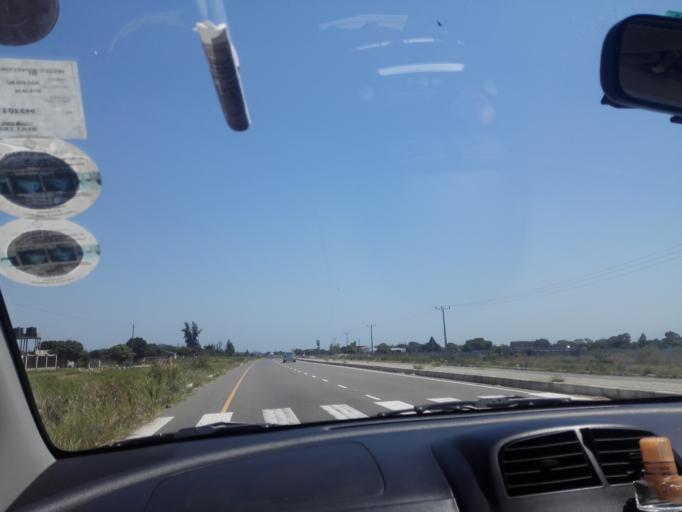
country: MZ
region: Maputo City
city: Maputo
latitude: -25.8069
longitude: 32.6721
